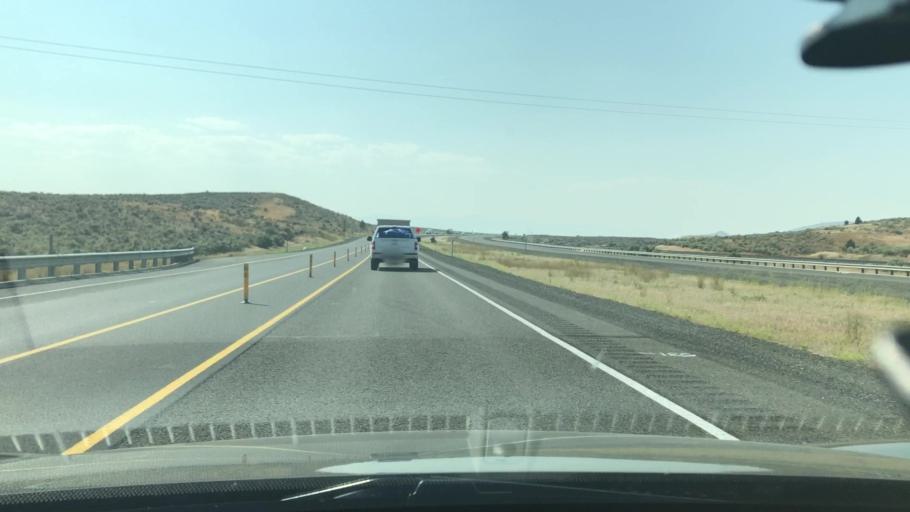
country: US
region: Oregon
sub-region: Baker County
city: Baker City
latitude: 44.6869
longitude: -117.6748
